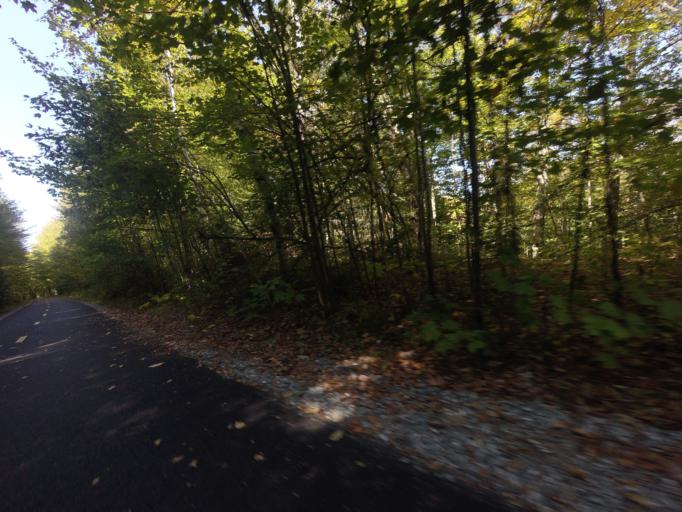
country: CA
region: Quebec
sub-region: Laurentides
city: Mont-Tremblant
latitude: 46.1343
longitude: -74.4793
